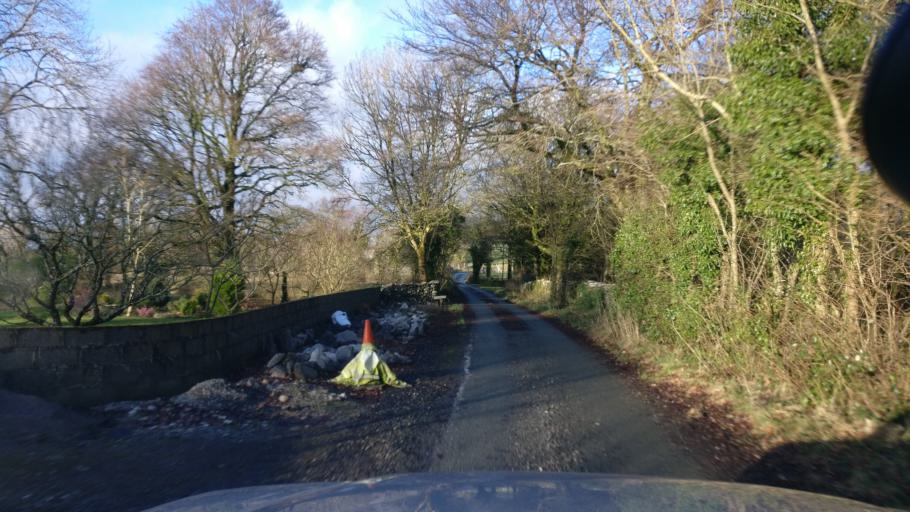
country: IE
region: Connaught
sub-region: County Galway
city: Loughrea
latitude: 53.2396
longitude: -8.5767
